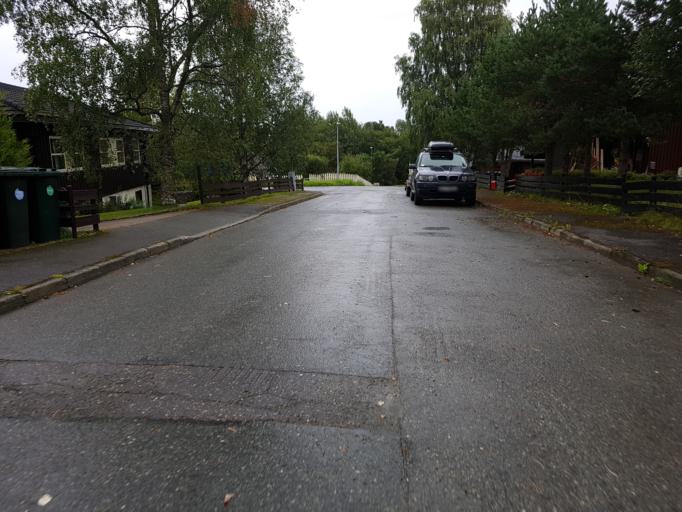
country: NO
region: Sor-Trondelag
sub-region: Trondheim
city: Trondheim
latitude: 63.4038
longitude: 10.4548
